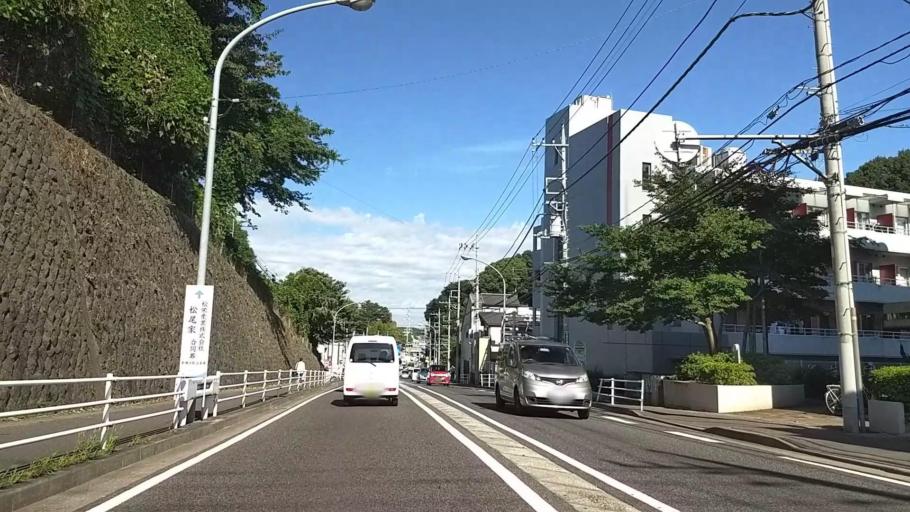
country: JP
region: Kanagawa
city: Yokohama
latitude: 35.4984
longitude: 139.6130
